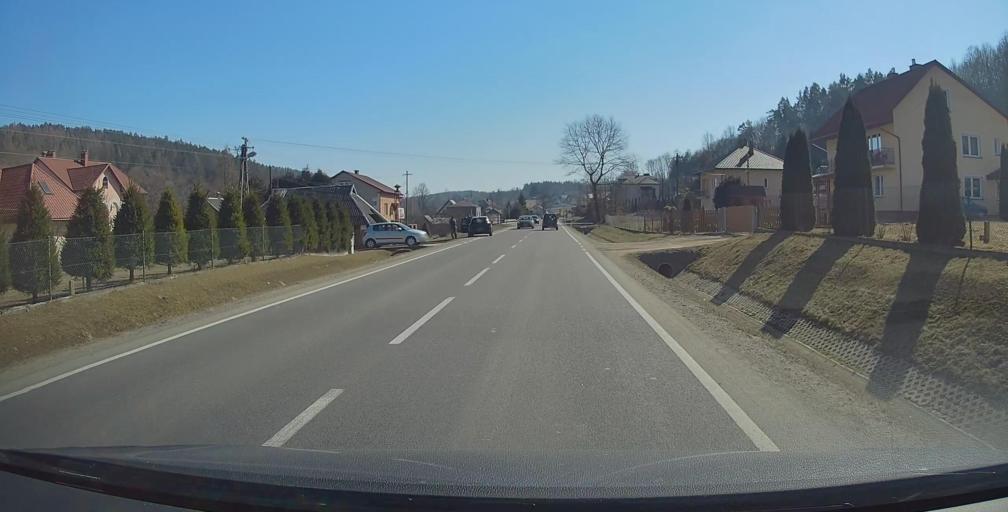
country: PL
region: Subcarpathian Voivodeship
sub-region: Powiat przemyski
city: Bircza
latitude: 49.6671
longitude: 22.4311
